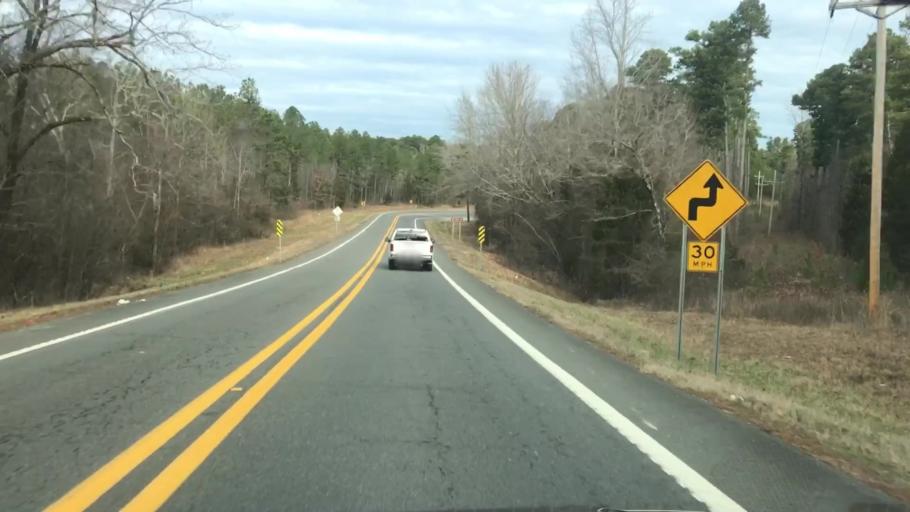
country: US
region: Arkansas
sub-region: Montgomery County
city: Mount Ida
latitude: 34.5914
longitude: -93.6649
